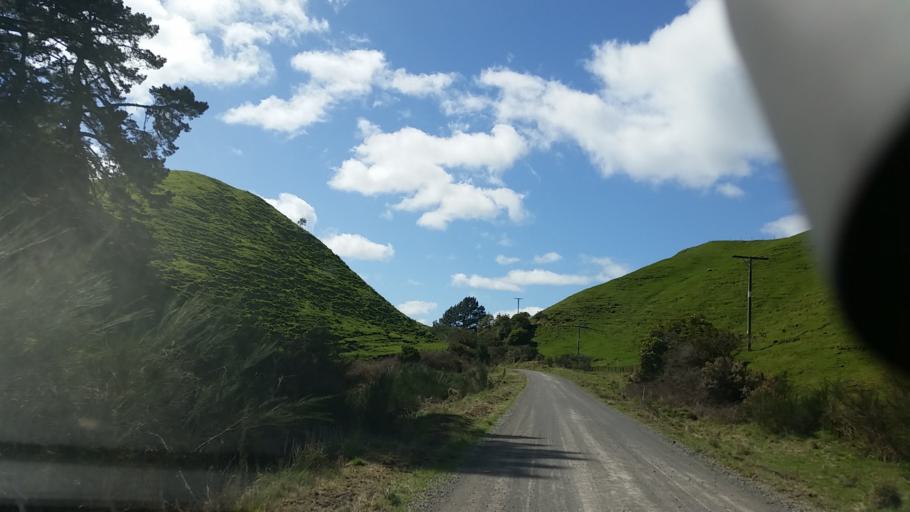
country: NZ
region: Waikato
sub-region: Taupo District
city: Taupo
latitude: -38.4785
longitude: 176.2171
